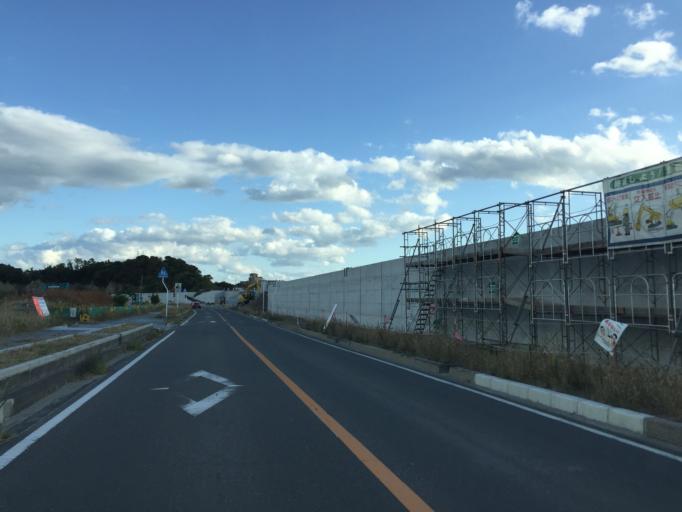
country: JP
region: Miyagi
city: Marumori
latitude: 37.8289
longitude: 140.9651
